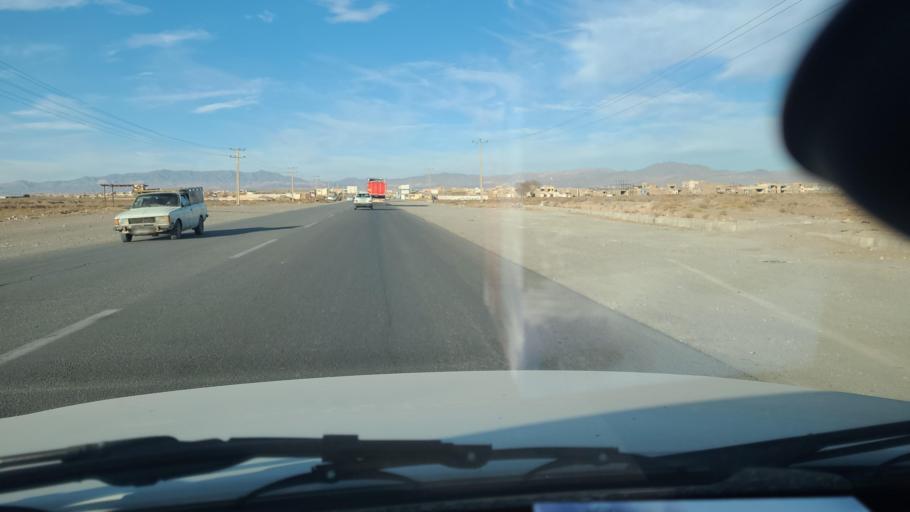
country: IR
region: Razavi Khorasan
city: Sabzevar
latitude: 36.2086
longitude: 57.6504
